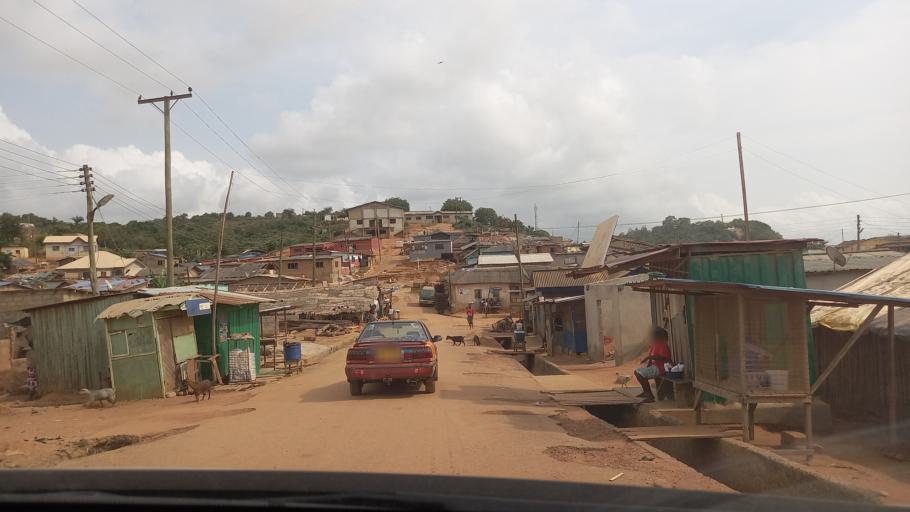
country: GH
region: Western
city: Shama Junction
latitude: 4.9857
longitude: -1.6379
